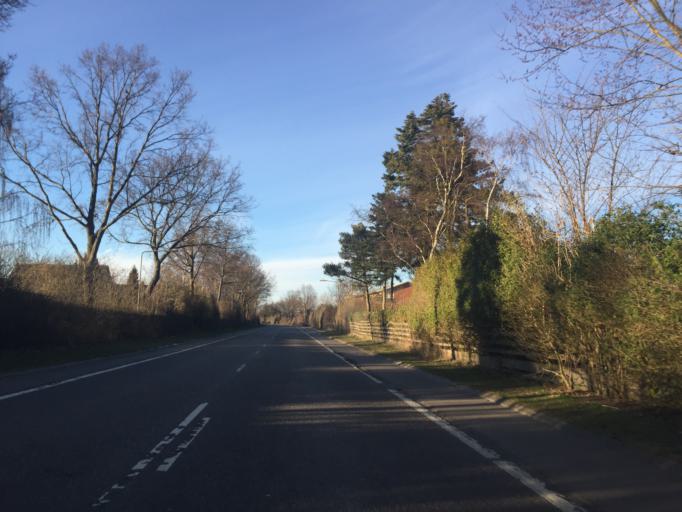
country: DK
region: Capital Region
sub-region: Dragor Kommune
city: Dragor
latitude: 55.5903
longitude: 12.6572
